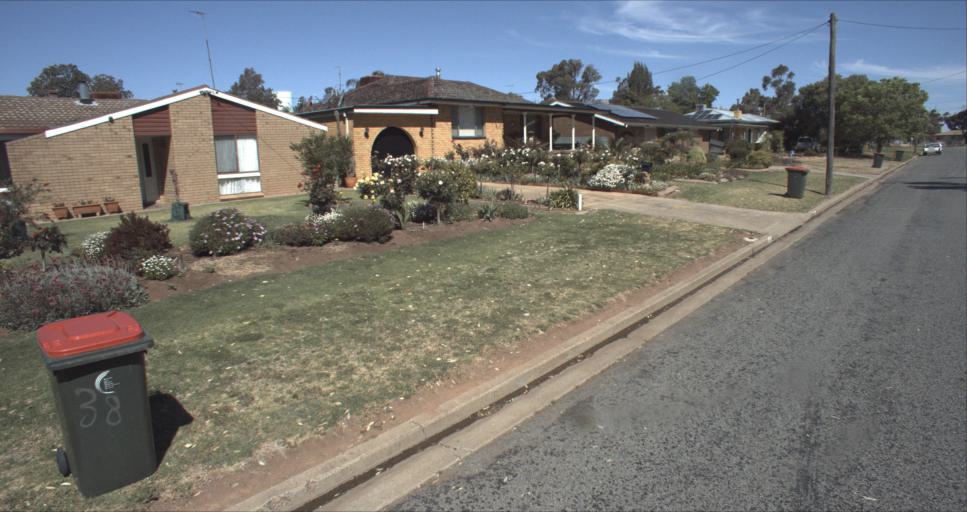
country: AU
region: New South Wales
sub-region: Leeton
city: Leeton
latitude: -34.5488
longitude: 146.3733
